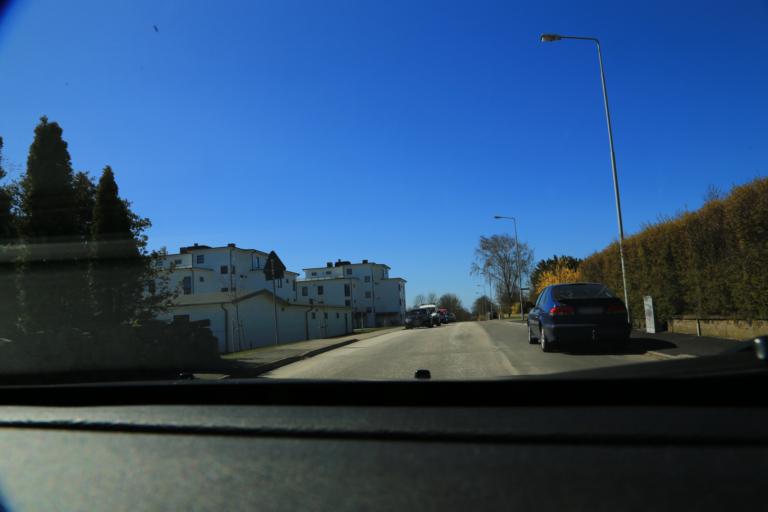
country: SE
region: Halland
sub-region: Varbergs Kommun
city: Varberg
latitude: 57.1022
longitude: 12.2838
